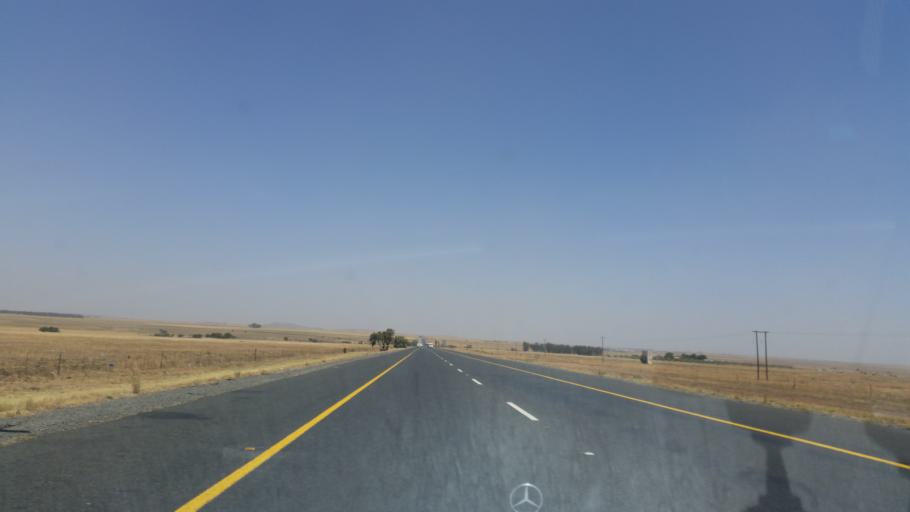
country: ZA
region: Orange Free State
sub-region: Lejweleputswa District Municipality
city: Brandfort
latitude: -28.7224
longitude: 26.7700
